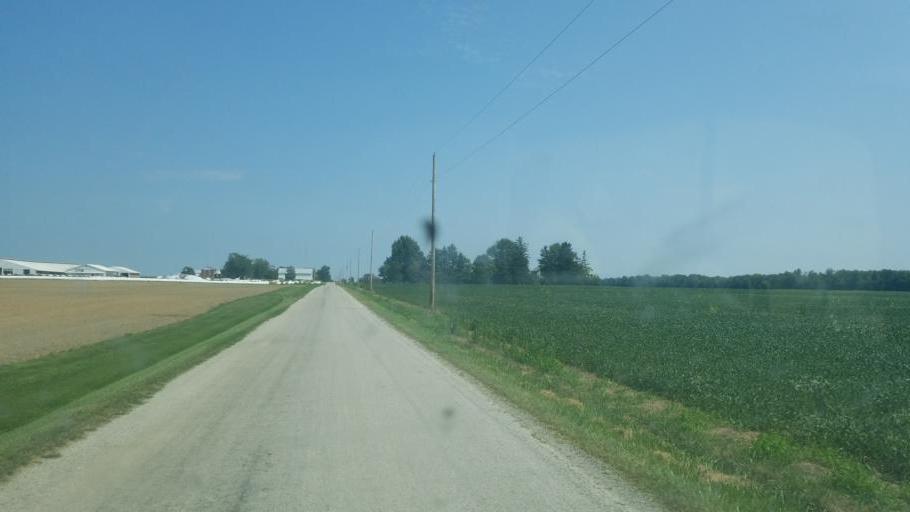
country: US
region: Ohio
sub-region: Crawford County
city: Bucyrus
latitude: 40.9358
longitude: -82.9764
